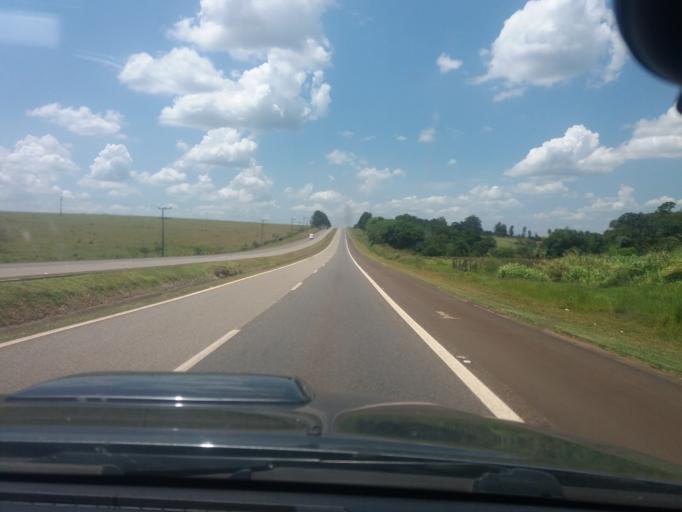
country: BR
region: Sao Paulo
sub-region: Itapetininga
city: Itapetininga
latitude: -23.5128
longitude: -47.9679
